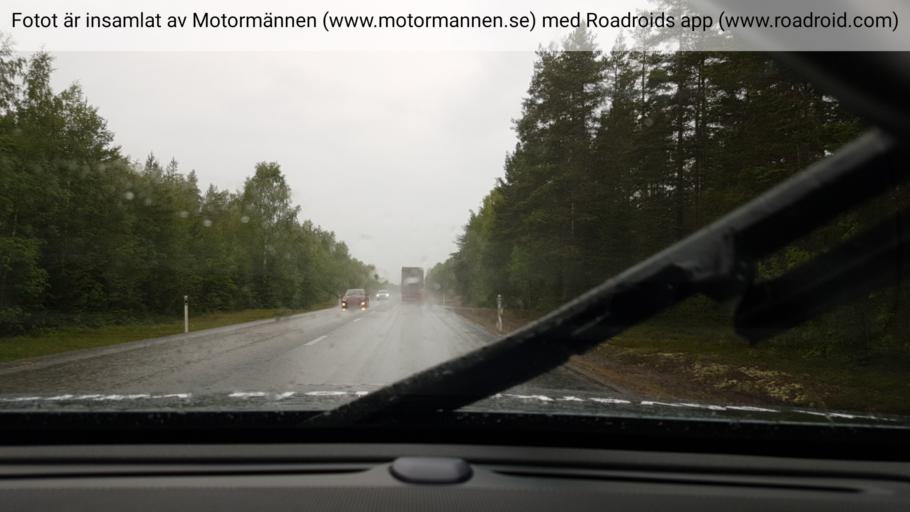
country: SE
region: Vaesterbotten
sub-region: Umea Kommun
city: Roback
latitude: 63.8517
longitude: 20.1121
